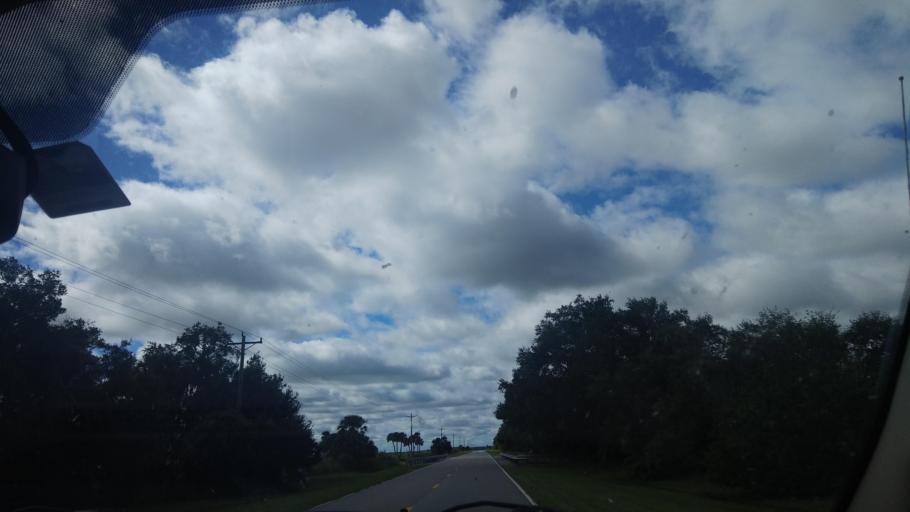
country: US
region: Florida
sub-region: Okeechobee County
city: Okeechobee
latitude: 27.3933
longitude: -80.9212
